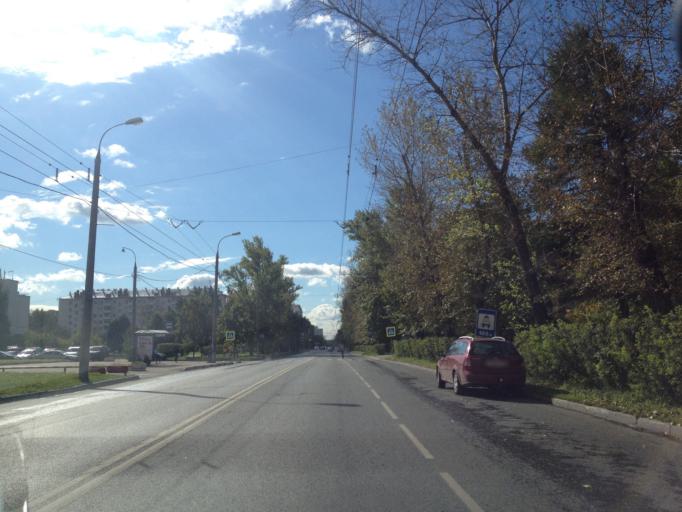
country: RU
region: Moscow
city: Metrogorodok
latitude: 55.8053
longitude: 37.7988
